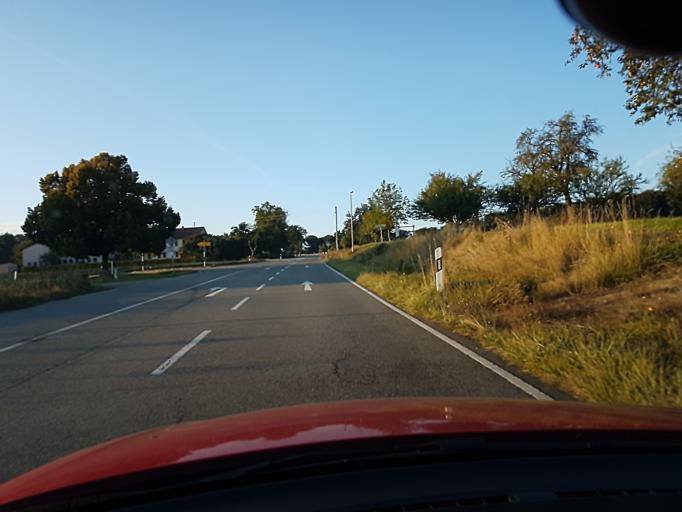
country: DE
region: Baden-Wuerttemberg
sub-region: Regierungsbezirk Stuttgart
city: Zaberfeld
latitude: 49.0793
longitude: 8.8954
